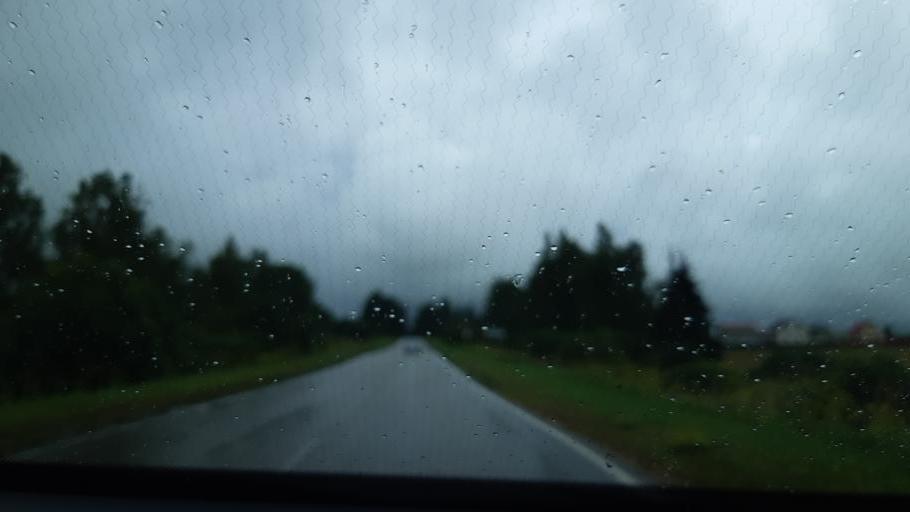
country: RU
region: Smolensk
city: Gagarin
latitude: 55.6258
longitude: 34.9638
